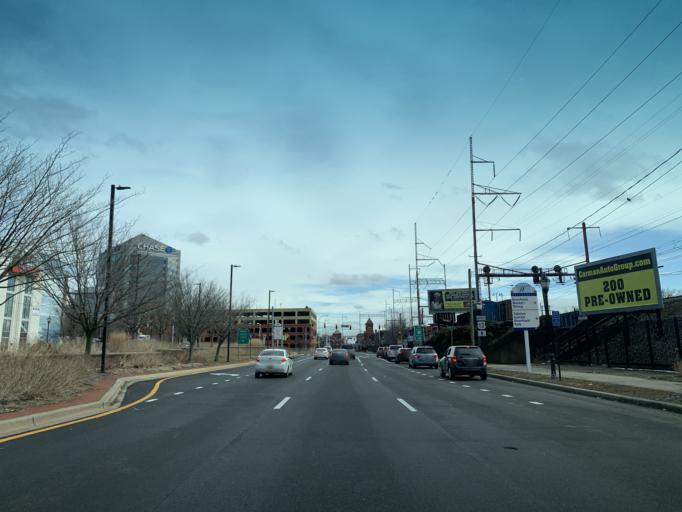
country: US
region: Delaware
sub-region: New Castle County
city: Wilmington
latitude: 39.7386
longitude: -75.5544
